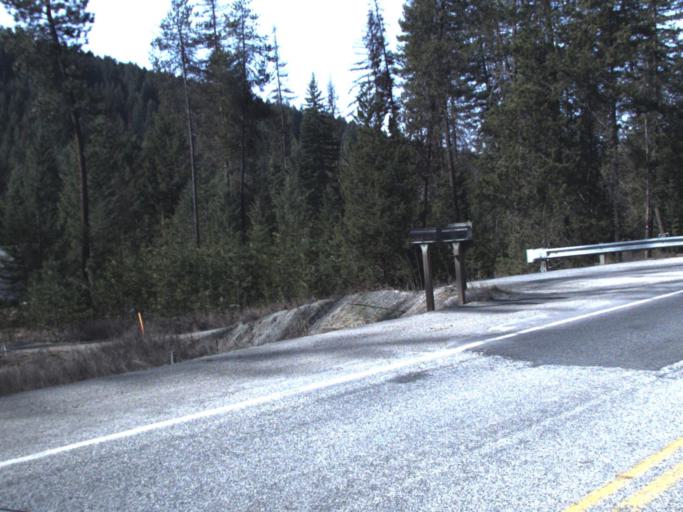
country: US
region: Washington
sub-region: Stevens County
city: Colville
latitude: 48.5404
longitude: -117.8382
